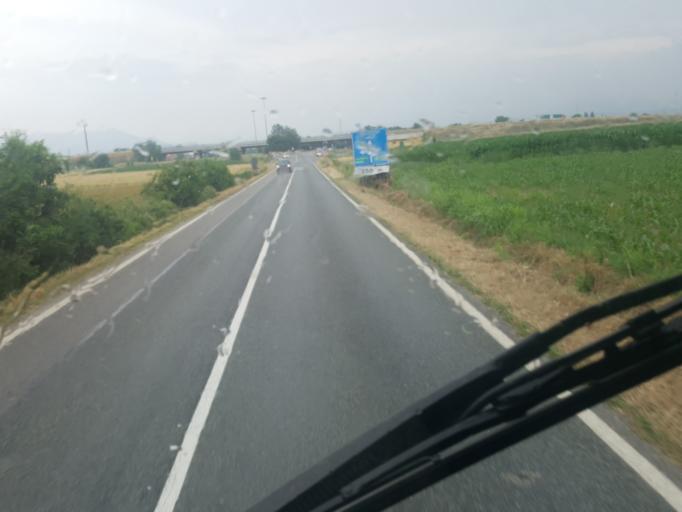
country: IT
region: Piedmont
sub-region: Provincia di Torino
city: Orbassano
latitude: 44.9782
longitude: 7.5566
